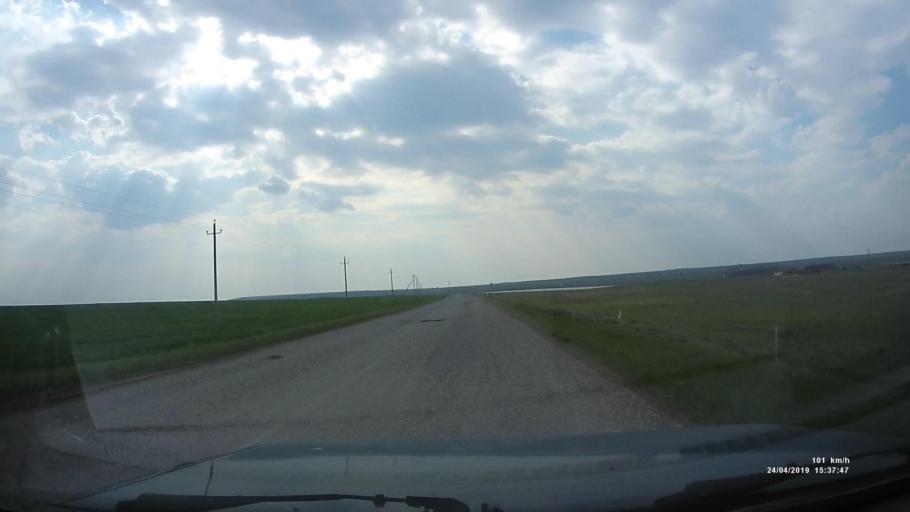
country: RU
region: Kalmykiya
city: Yashalta
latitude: 46.6000
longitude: 42.8411
